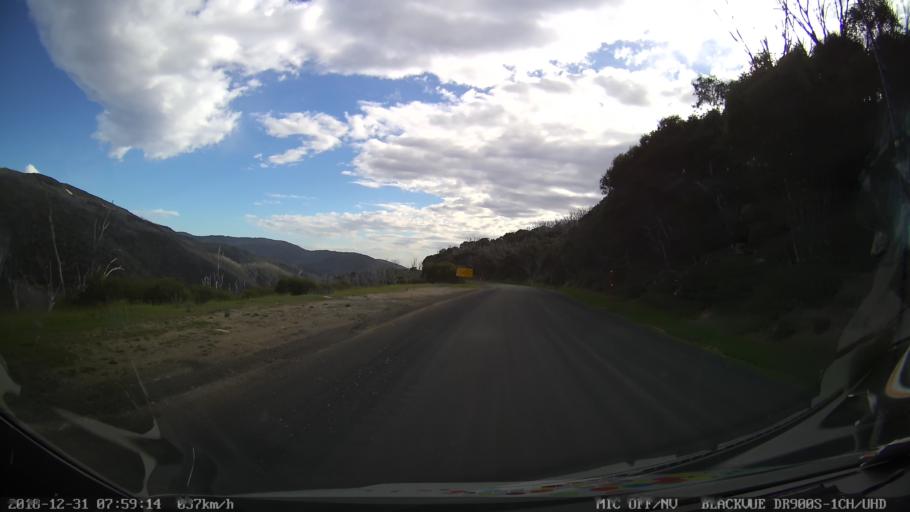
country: AU
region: New South Wales
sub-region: Snowy River
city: Jindabyne
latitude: -36.3720
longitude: 148.3842
